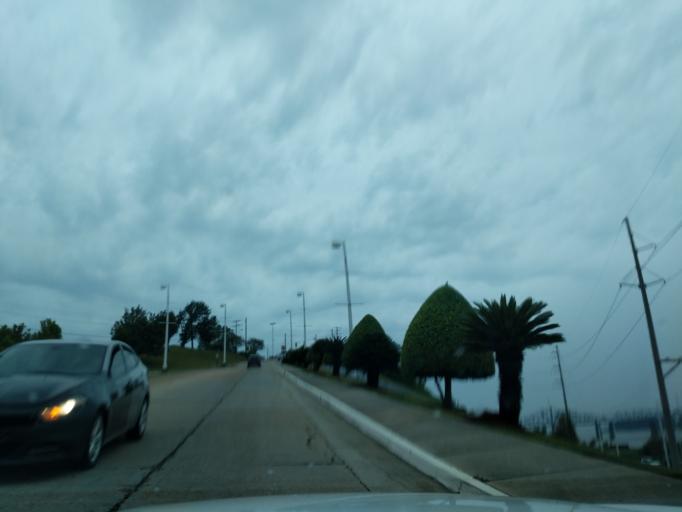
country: US
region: Mississippi
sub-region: Warren County
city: Vicksburg
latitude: 32.3243
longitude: -90.8953
